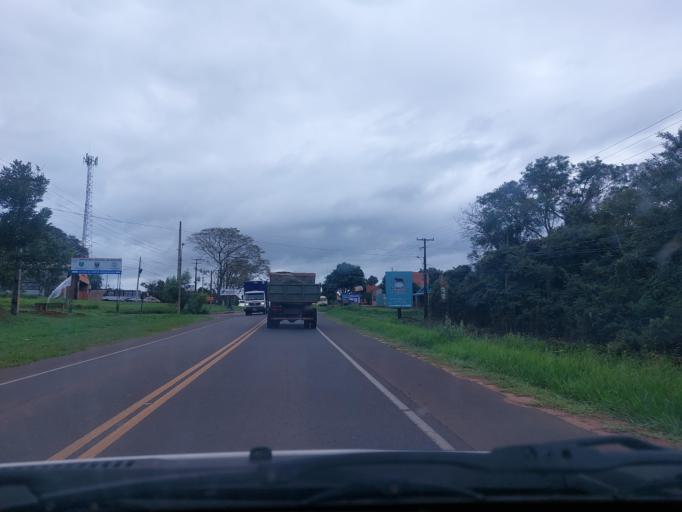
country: PY
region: San Pedro
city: Guayaybi
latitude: -24.6638
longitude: -56.4179
